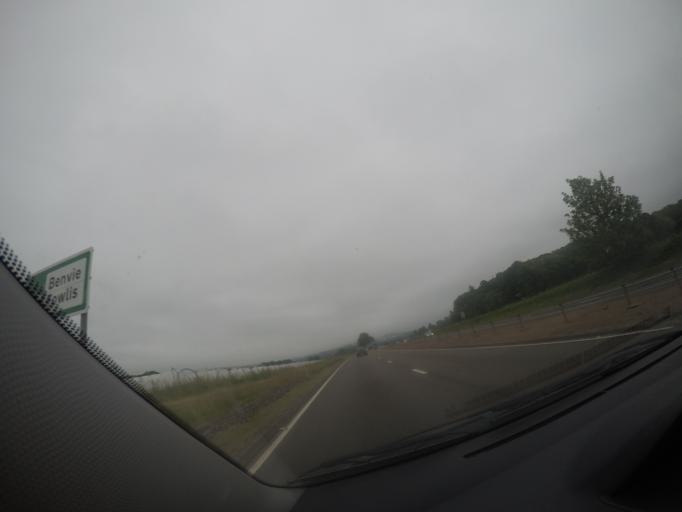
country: GB
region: Scotland
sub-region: Angus
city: Muirhead
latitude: 56.4617
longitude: -3.0914
